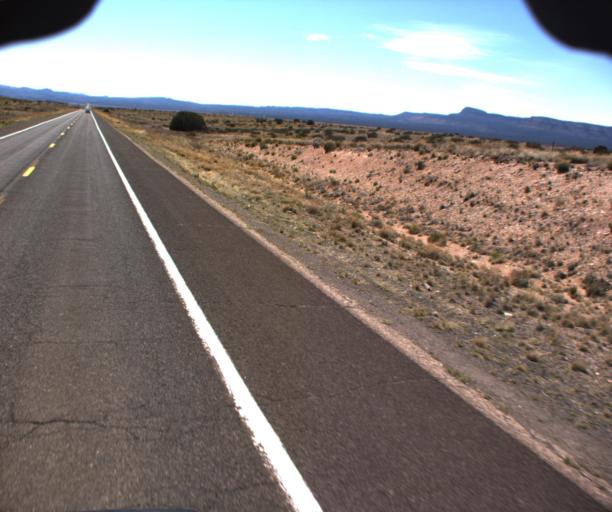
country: US
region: Arizona
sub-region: Mohave County
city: Peach Springs
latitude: 35.5142
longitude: -113.5026
